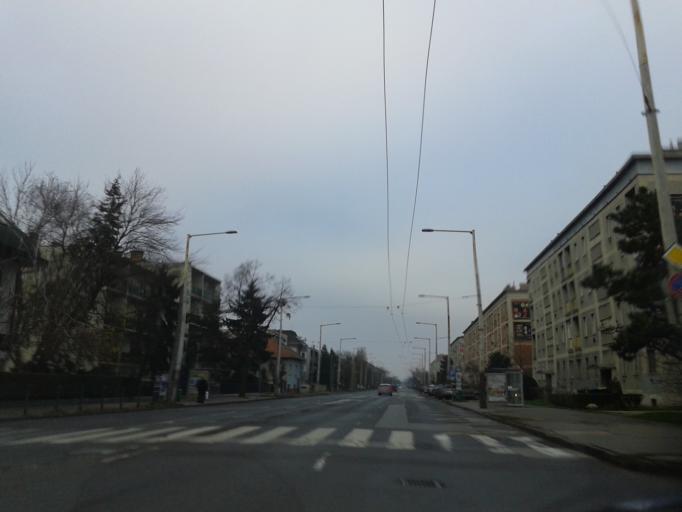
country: HU
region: Budapest
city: Budapest XIV. keruelet
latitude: 47.5059
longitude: 19.1230
